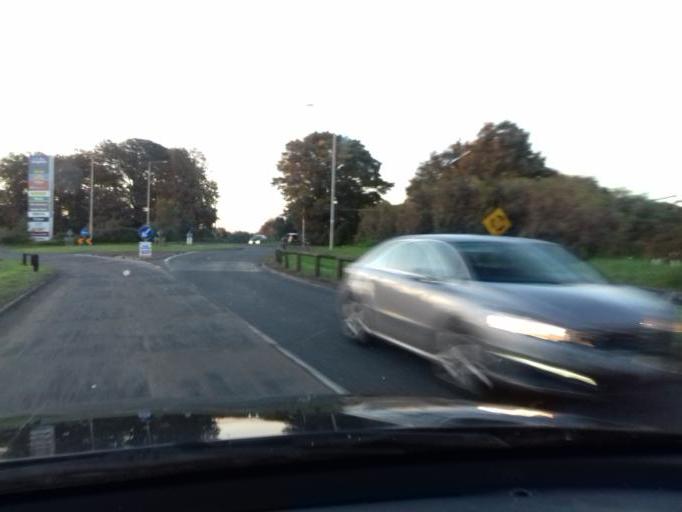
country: IE
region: Leinster
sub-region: Lu
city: Drogheda
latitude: 53.7272
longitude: -6.3844
